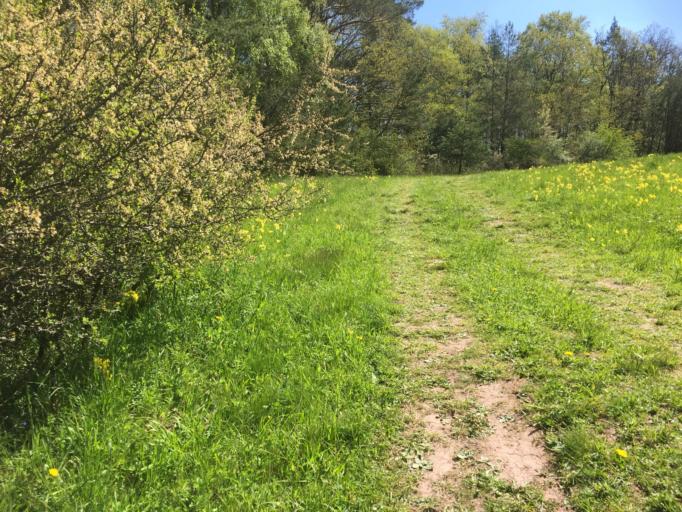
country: DE
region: Bavaria
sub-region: Regierungsbezirk Unterfranken
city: Sulzfeld
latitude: 50.2711
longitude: 10.4230
